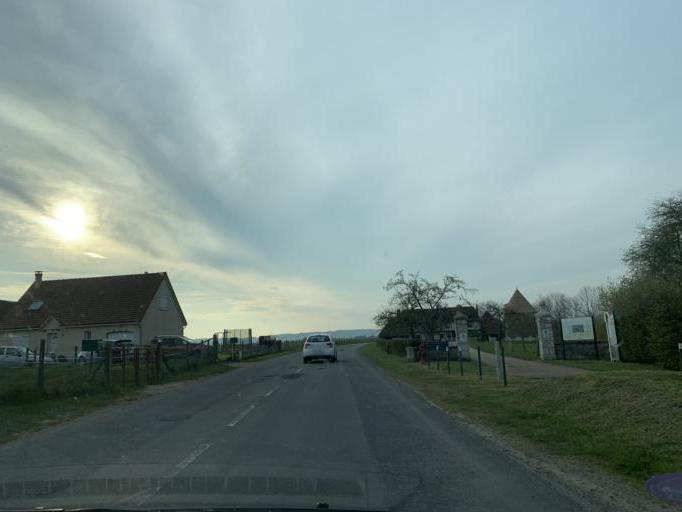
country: FR
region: Haute-Normandie
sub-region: Departement de la Seine-Maritime
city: La Mailleraye-sur-Seine
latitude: 49.4971
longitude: 0.7586
